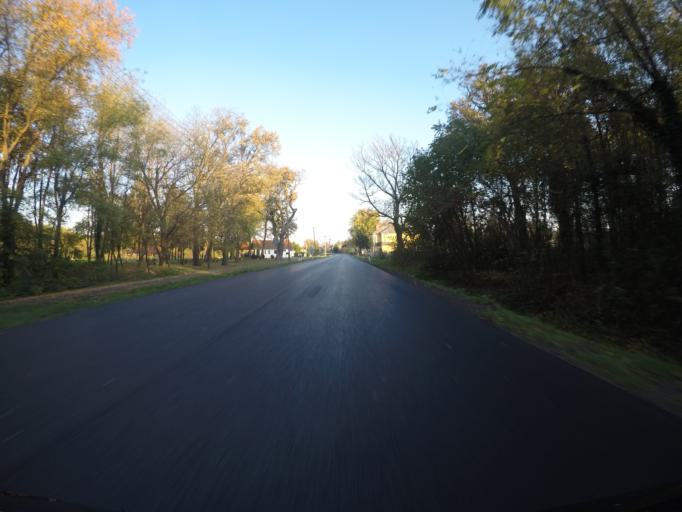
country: HU
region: Somogy
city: Barcs
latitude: 45.9796
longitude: 17.5826
